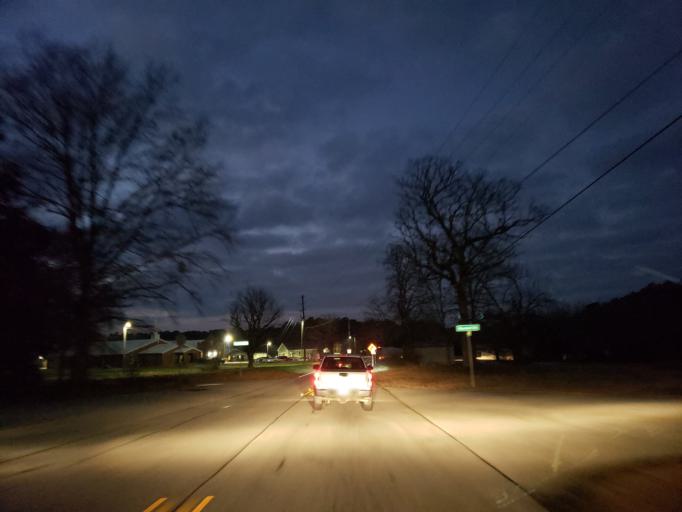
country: US
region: Georgia
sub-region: Polk County
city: Rockmart
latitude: 33.9242
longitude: -84.9952
